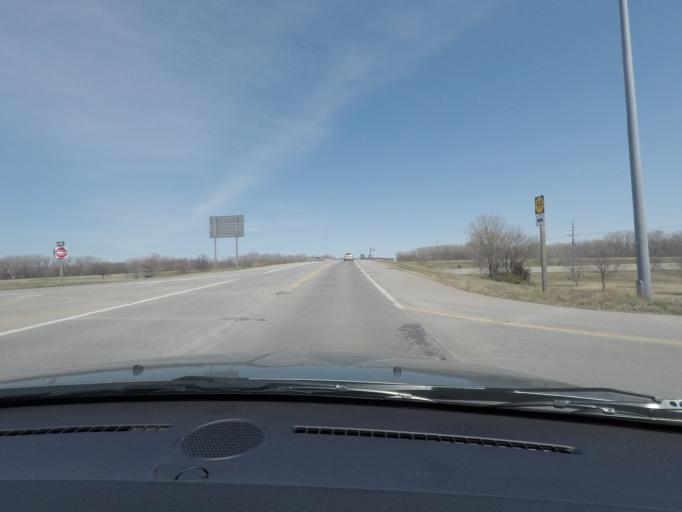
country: US
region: Kansas
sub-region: Lyon County
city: Emporia
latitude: 38.4221
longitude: -96.1817
